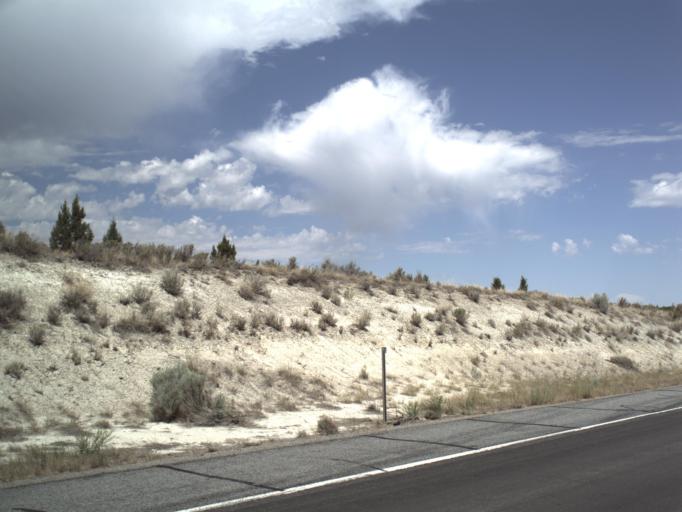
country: US
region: Utah
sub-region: Utah County
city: Eagle Mountain
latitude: 40.0007
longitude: -112.2745
